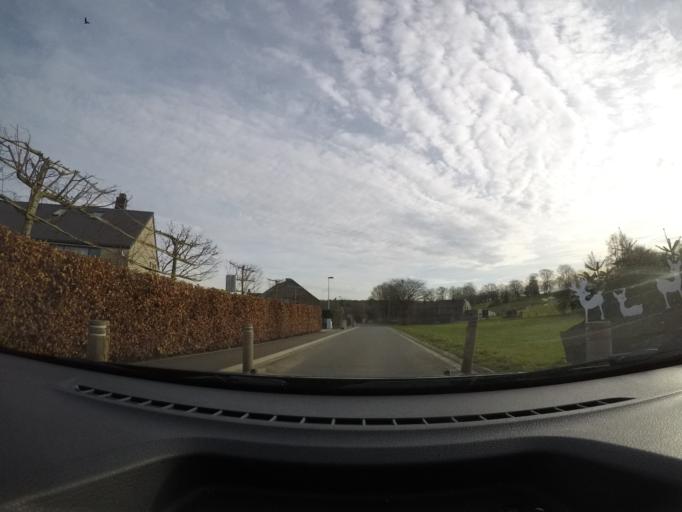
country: BE
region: Wallonia
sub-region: Province du Luxembourg
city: Leglise
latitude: 49.8283
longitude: 5.4892
